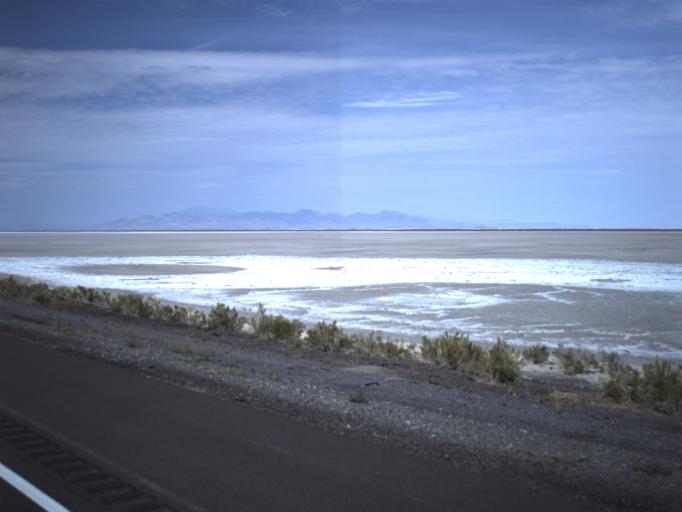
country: US
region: Utah
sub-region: Tooele County
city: Wendover
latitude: 40.7290
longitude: -113.3774
